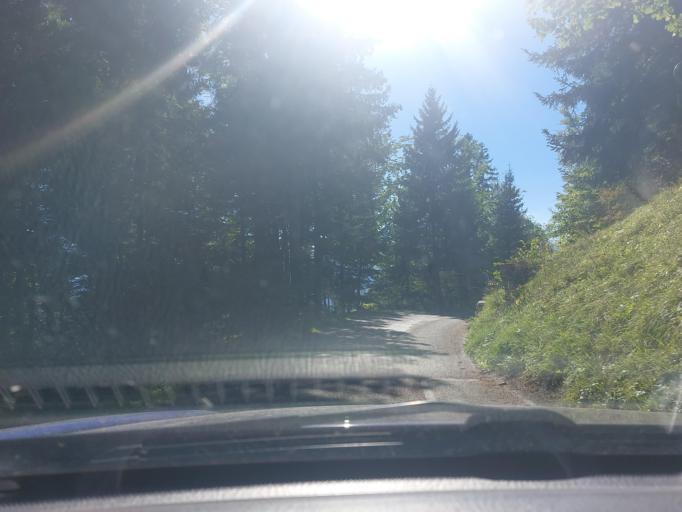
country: CH
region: Vaud
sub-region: Aigle District
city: Aigle
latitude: 46.3573
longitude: 6.9732
